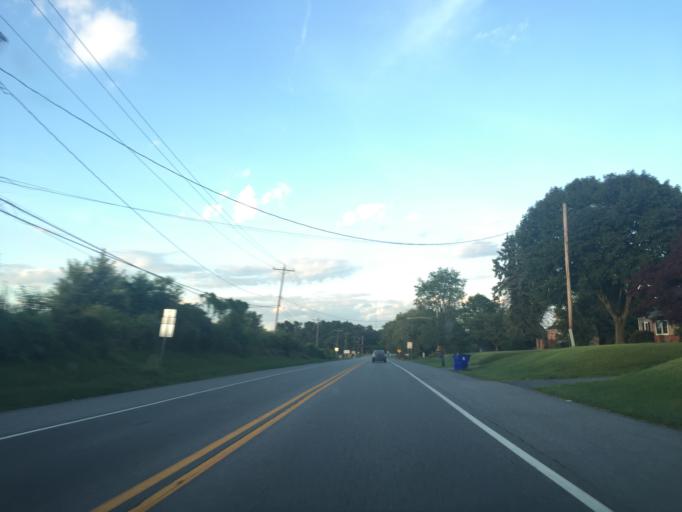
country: US
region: Delaware
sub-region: New Castle County
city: Middletown
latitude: 39.4570
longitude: -75.6688
